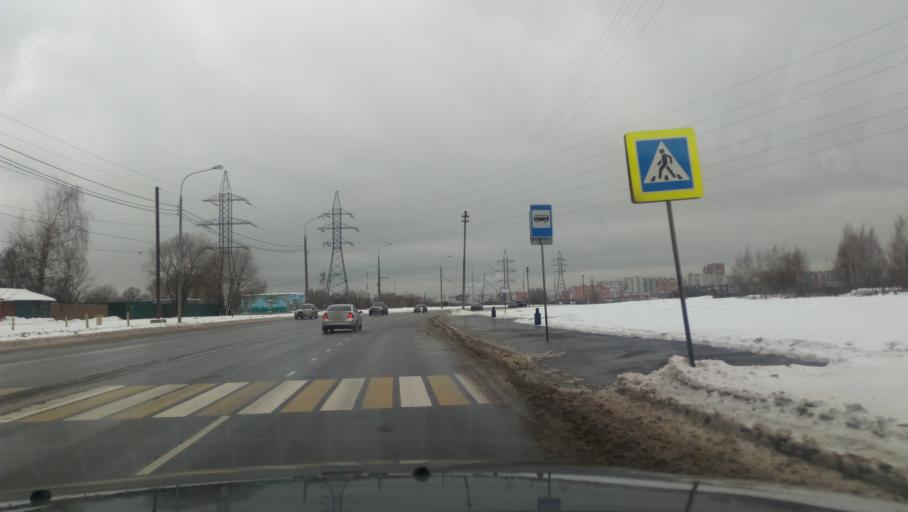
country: RU
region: Moscow
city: Zhulebino
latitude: 55.7226
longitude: 37.8604
